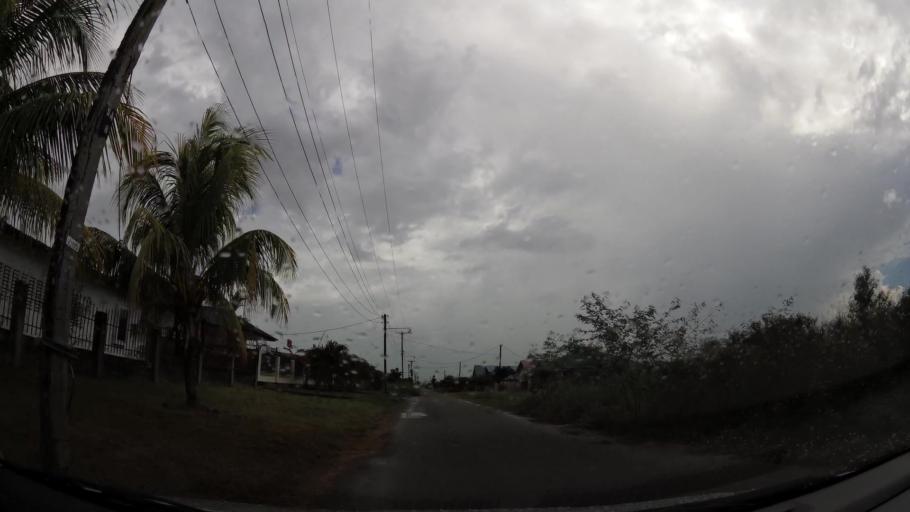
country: SR
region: Commewijne
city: Nieuw Amsterdam
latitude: 5.8624
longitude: -55.1147
